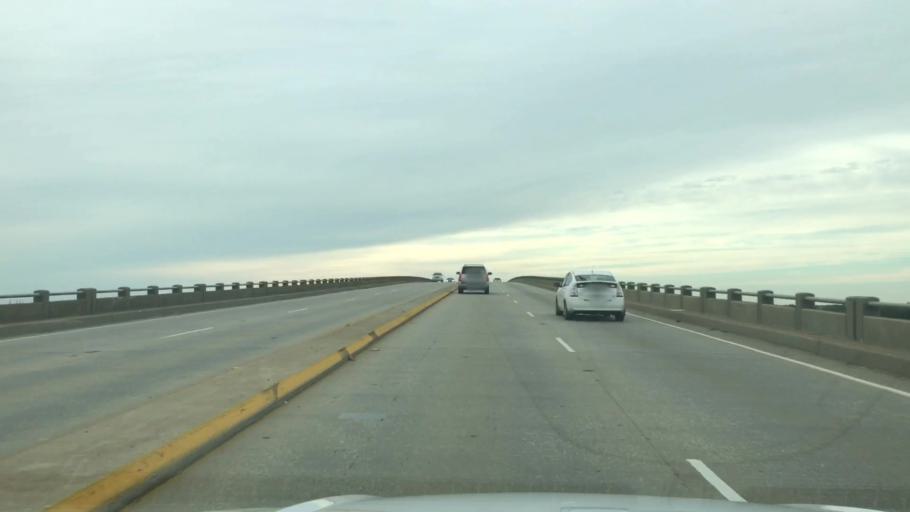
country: US
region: South Carolina
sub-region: Georgetown County
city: Georgetown
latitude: 33.3656
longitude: -79.2504
